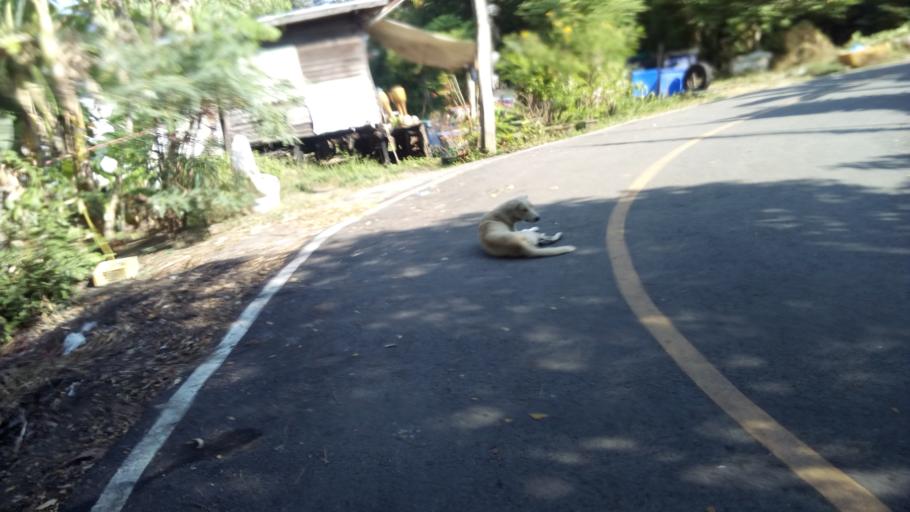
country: TH
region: Pathum Thani
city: Ban Rangsit
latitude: 14.0513
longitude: 100.8241
